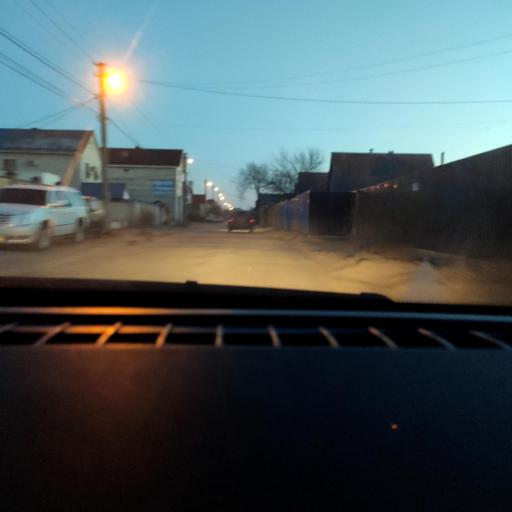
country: RU
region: Voronezj
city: Podgornoye
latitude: 51.7432
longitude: 39.1626
